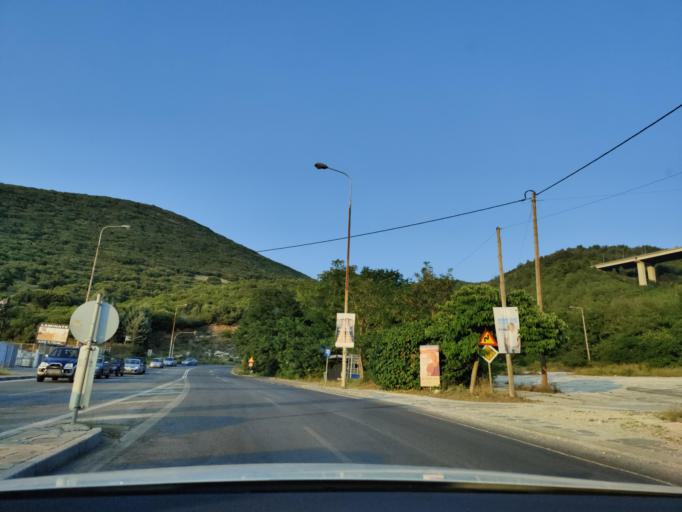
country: GR
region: East Macedonia and Thrace
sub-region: Nomos Kavalas
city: Amygdaleonas
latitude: 40.9507
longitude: 24.3702
